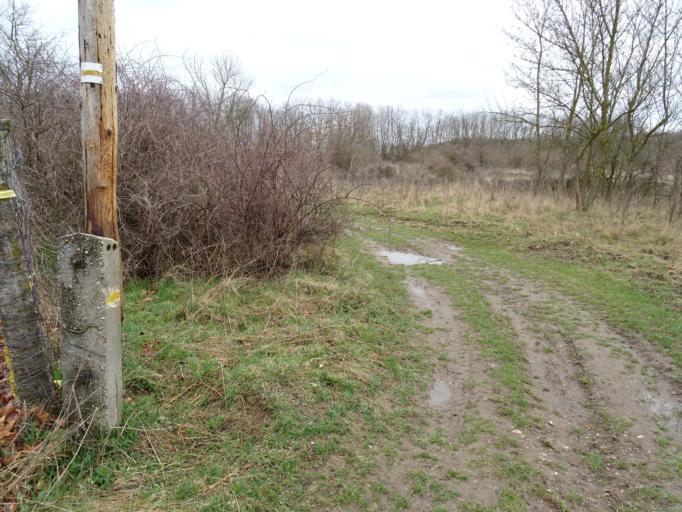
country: HU
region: Gyor-Moson-Sopron
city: Fertoszentmiklos
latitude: 47.4862
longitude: 16.8319
